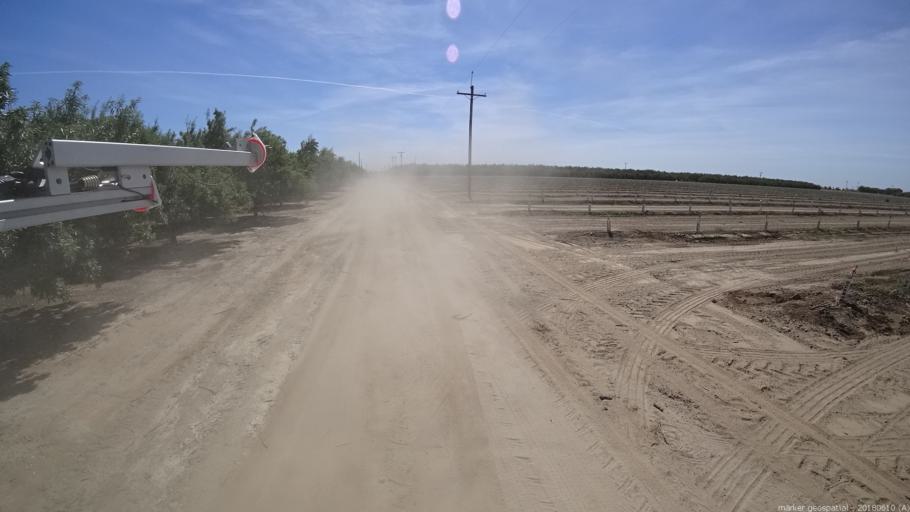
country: US
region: California
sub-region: Madera County
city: Chowchilla
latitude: 37.0253
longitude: -120.3855
